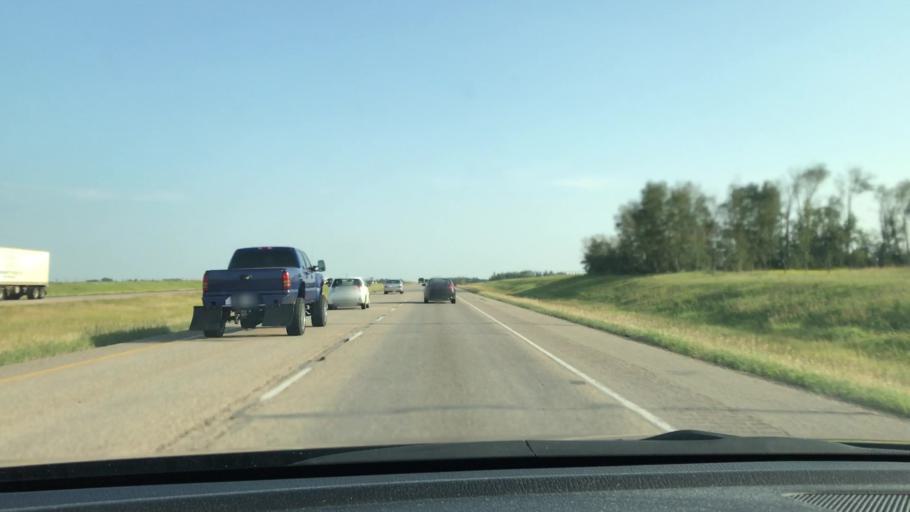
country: CA
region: Alberta
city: Millet
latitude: 53.1277
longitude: -113.5985
